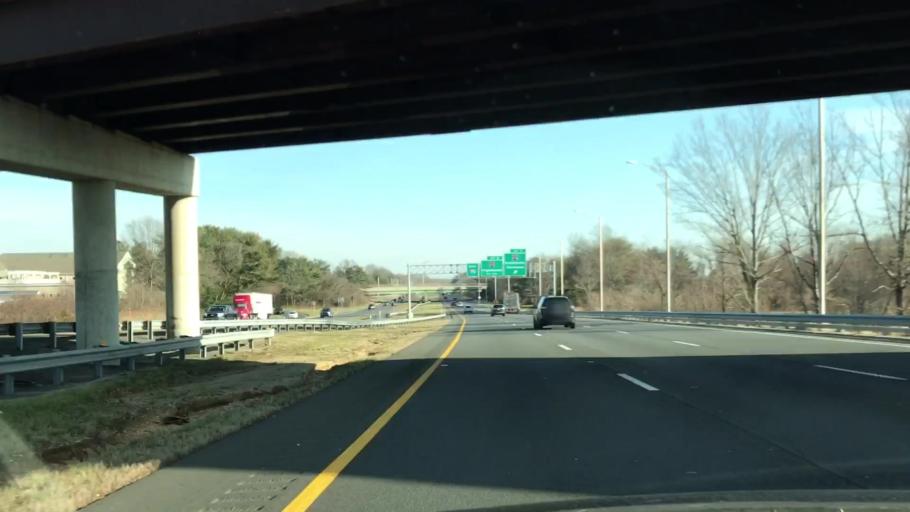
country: US
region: New Jersey
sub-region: Monmouth County
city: Allentown
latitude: 40.1926
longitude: -74.5973
